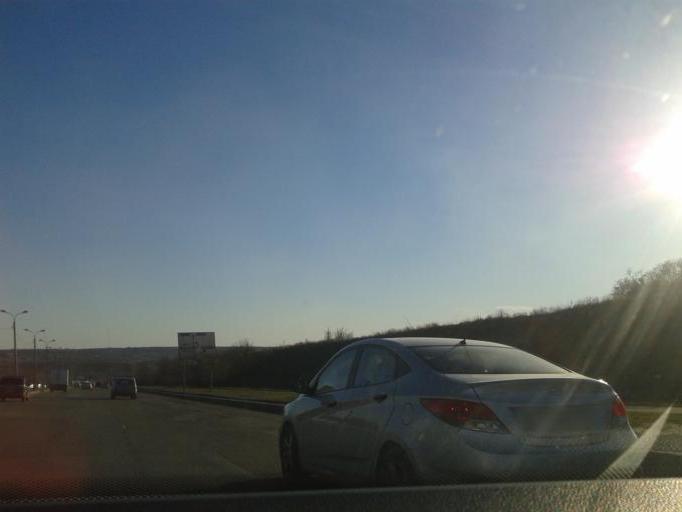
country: RU
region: Volgograd
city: Volgograd
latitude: 48.7386
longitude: 44.4598
